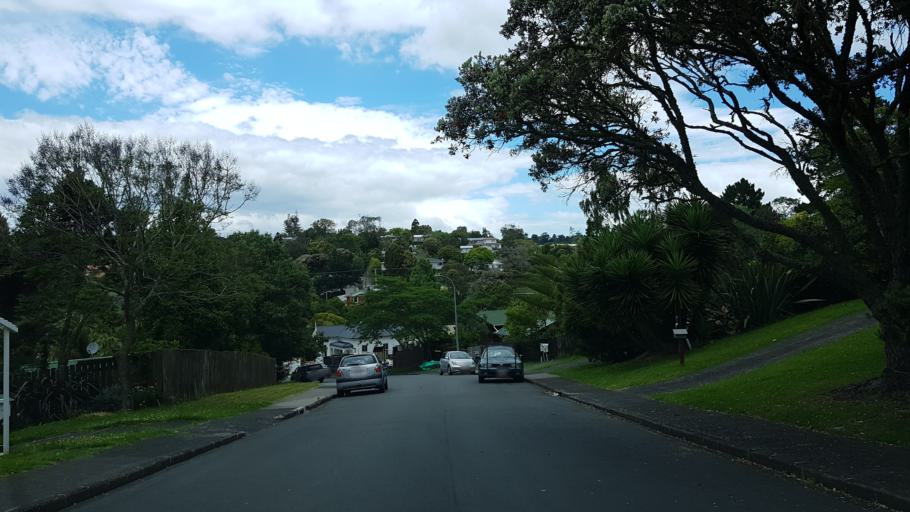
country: NZ
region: Auckland
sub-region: Auckland
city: North Shore
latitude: -36.7940
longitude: 174.6957
